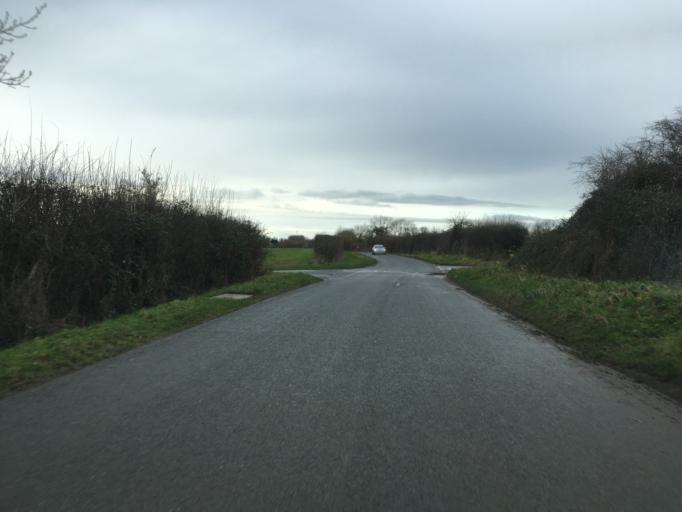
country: GB
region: England
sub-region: Gloucestershire
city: Gotherington
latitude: 52.0302
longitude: -2.0150
